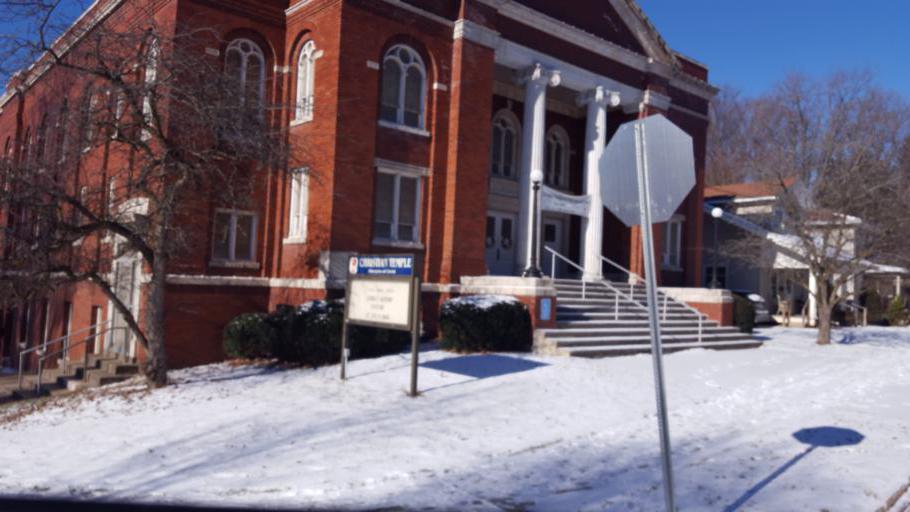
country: US
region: New York
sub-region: Allegany County
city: Wellsville
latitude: 42.1219
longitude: -77.9444
